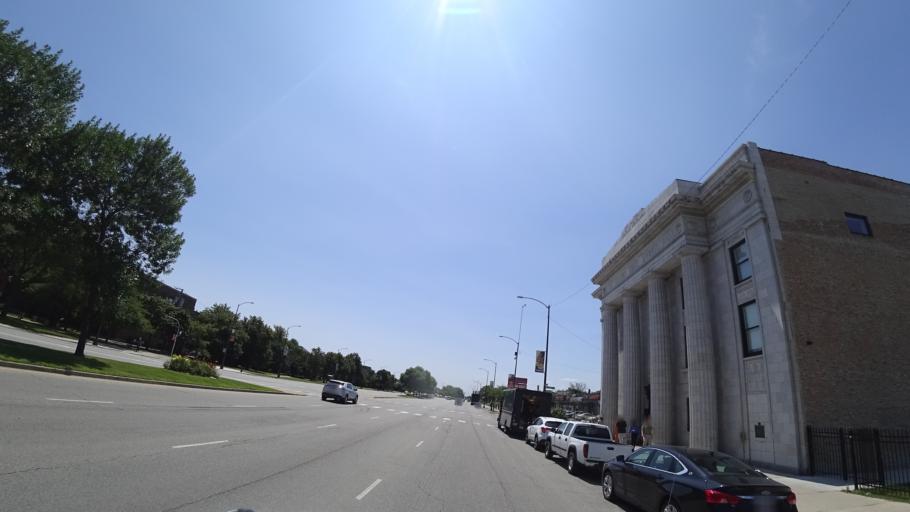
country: US
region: Illinois
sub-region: Cook County
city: Chicago
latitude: 41.7718
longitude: -87.5865
